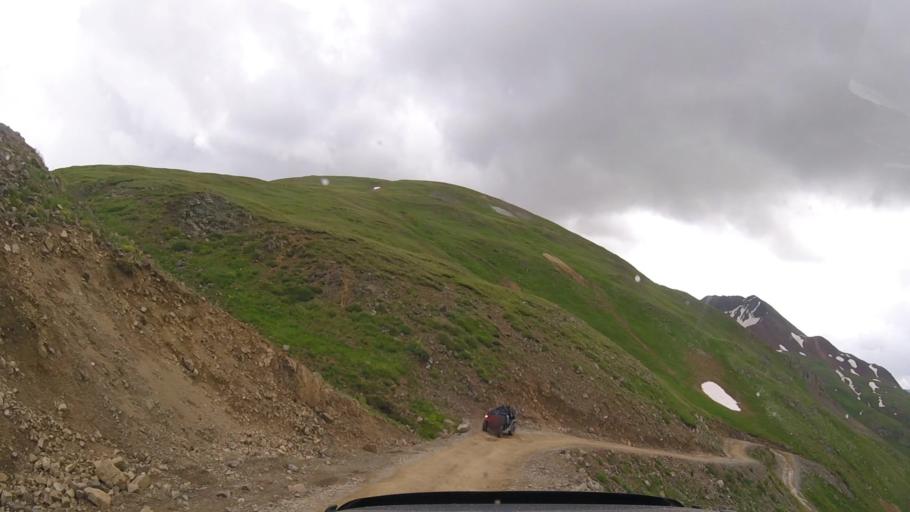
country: US
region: Colorado
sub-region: Ouray County
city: Ouray
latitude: 37.9612
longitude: -107.5758
